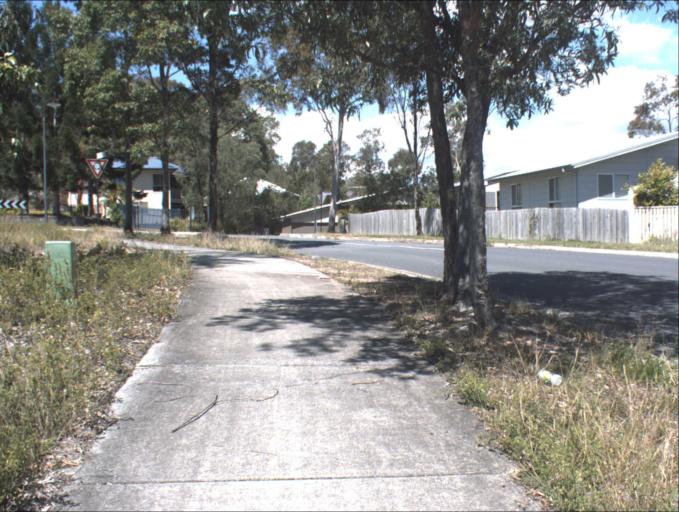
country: AU
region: Queensland
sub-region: Logan
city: Waterford West
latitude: -27.7083
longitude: 153.1574
